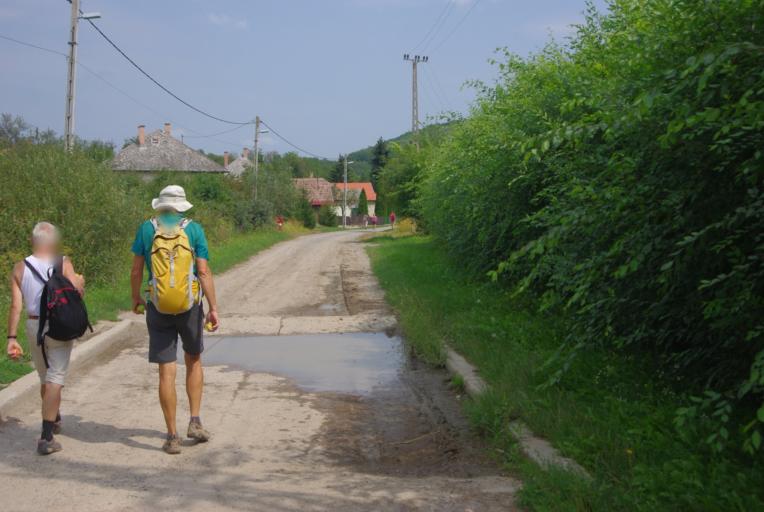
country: HU
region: Nograd
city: Rimoc
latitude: 48.0066
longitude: 19.4933
